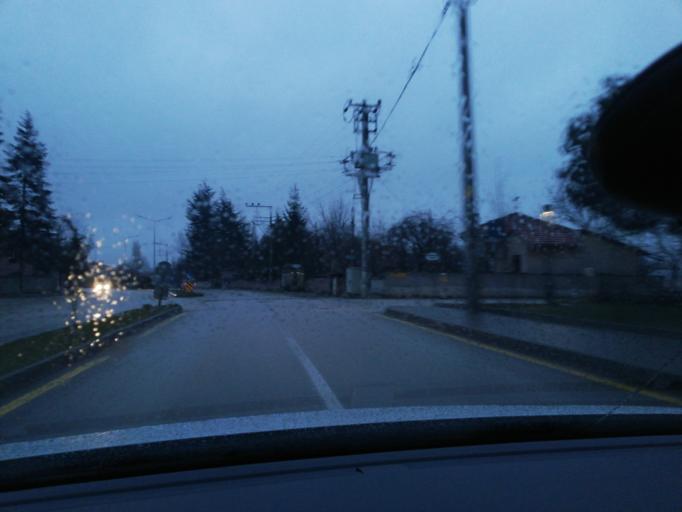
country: TR
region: Bolu
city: Bolu
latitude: 40.7314
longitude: 31.5694
